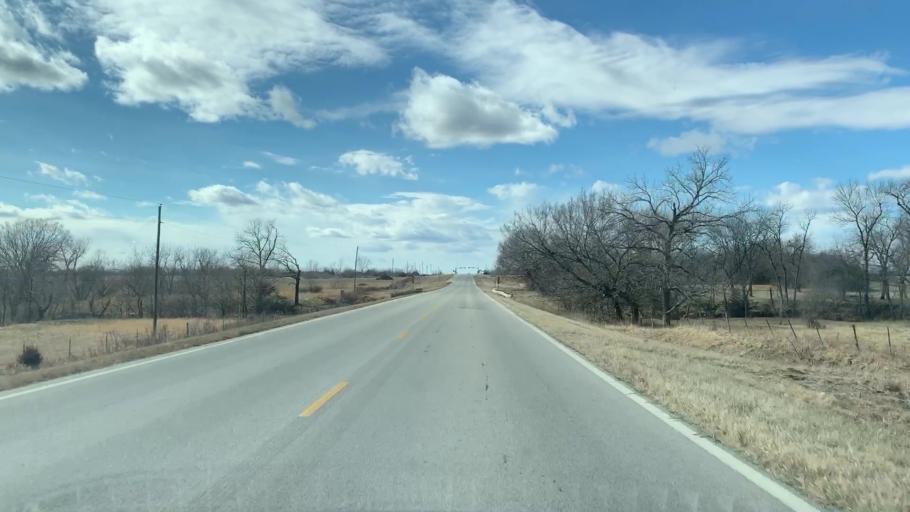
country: US
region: Kansas
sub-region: Neosho County
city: Chanute
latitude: 37.5288
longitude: -95.4626
